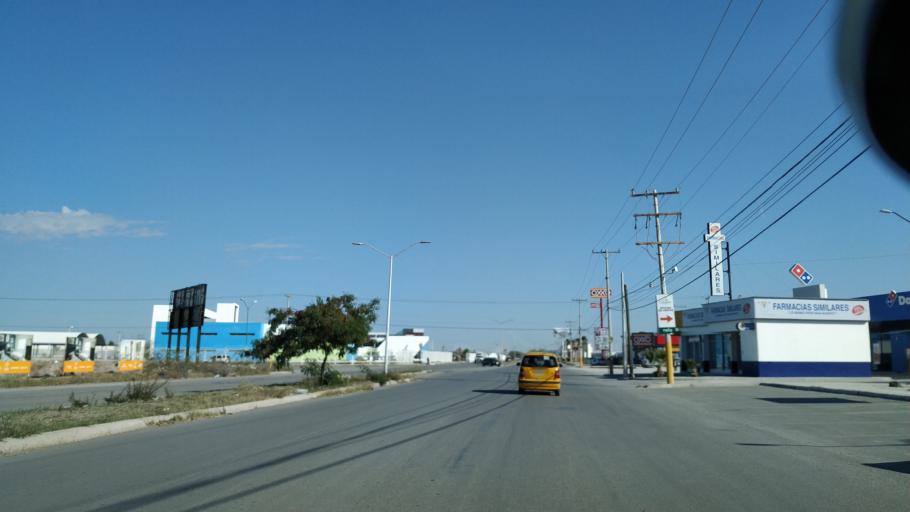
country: MX
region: Coahuila
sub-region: Torreon
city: Fraccionamiento la Noria
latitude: 25.5393
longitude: -103.3481
